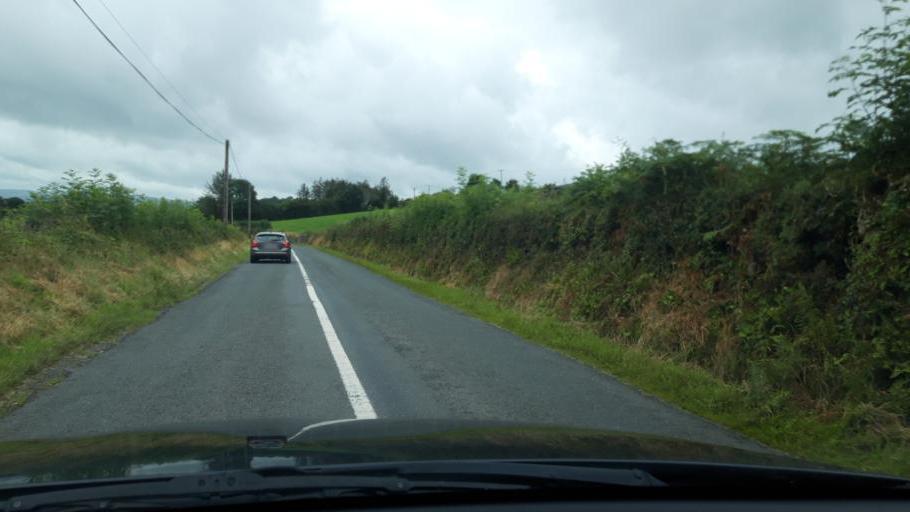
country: IE
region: Munster
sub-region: County Cork
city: Youghal
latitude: 52.1640
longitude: -7.8492
